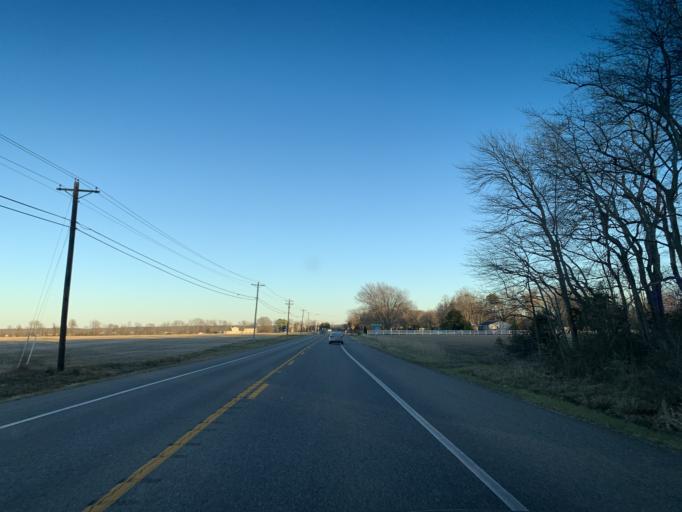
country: US
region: Maryland
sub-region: Saint Mary's County
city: Golden Beach
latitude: 38.5164
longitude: -76.6849
